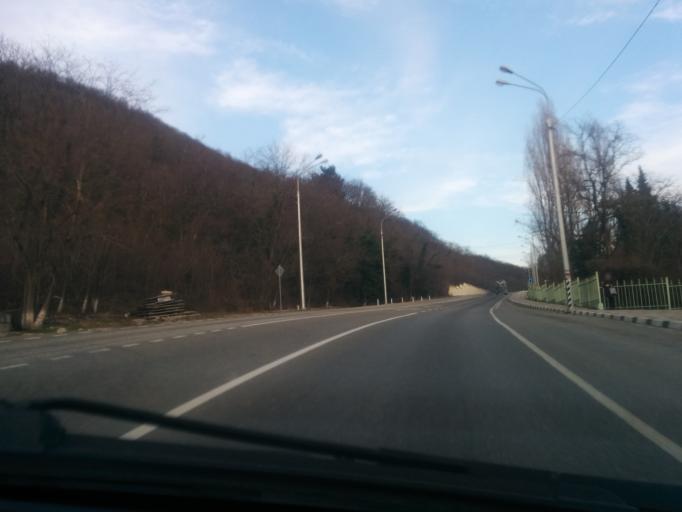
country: RU
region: Krasnodarskiy
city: Nebug
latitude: 44.1772
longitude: 38.9463
